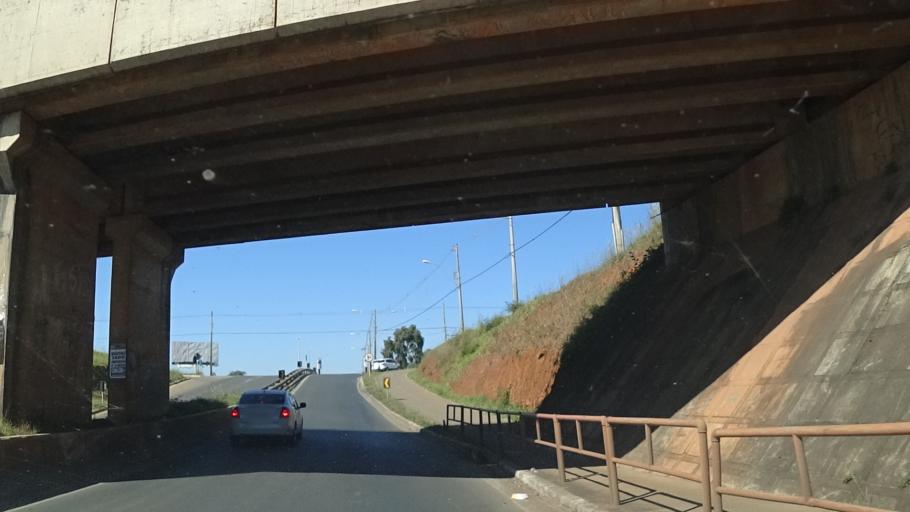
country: BR
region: Federal District
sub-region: Brasilia
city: Brasilia
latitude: -15.8373
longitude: -48.0040
